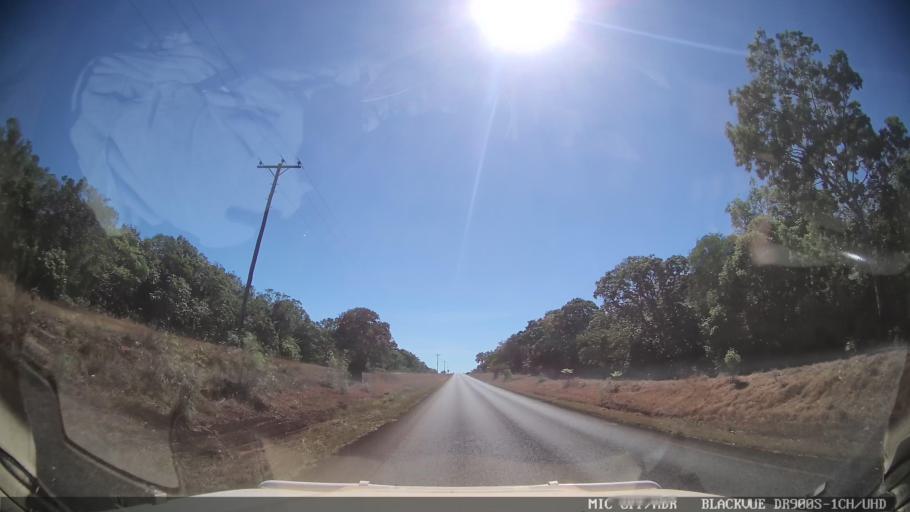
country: AU
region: Queensland
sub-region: Torres
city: Thursday Island
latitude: -10.9038
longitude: 142.3320
